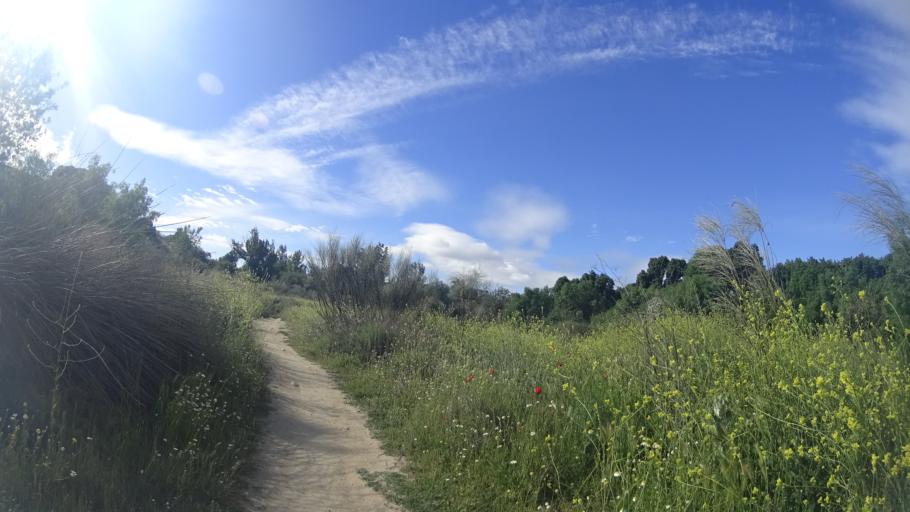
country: ES
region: Madrid
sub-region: Provincia de Madrid
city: Villanueva del Pardillo
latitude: 40.5136
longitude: -3.9391
